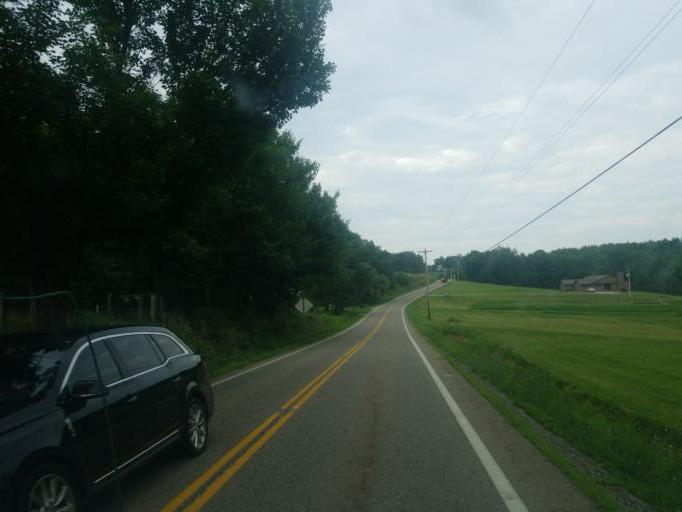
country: US
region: Ohio
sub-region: Carroll County
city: Lake Mohawk
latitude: 40.6387
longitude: -81.2208
